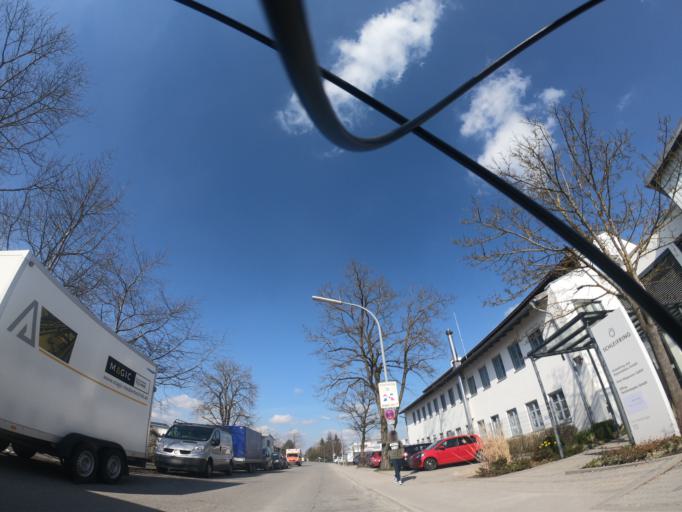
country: DE
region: Bavaria
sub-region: Upper Bavaria
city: Fuerstenfeldbruck
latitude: 48.1944
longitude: 11.2515
